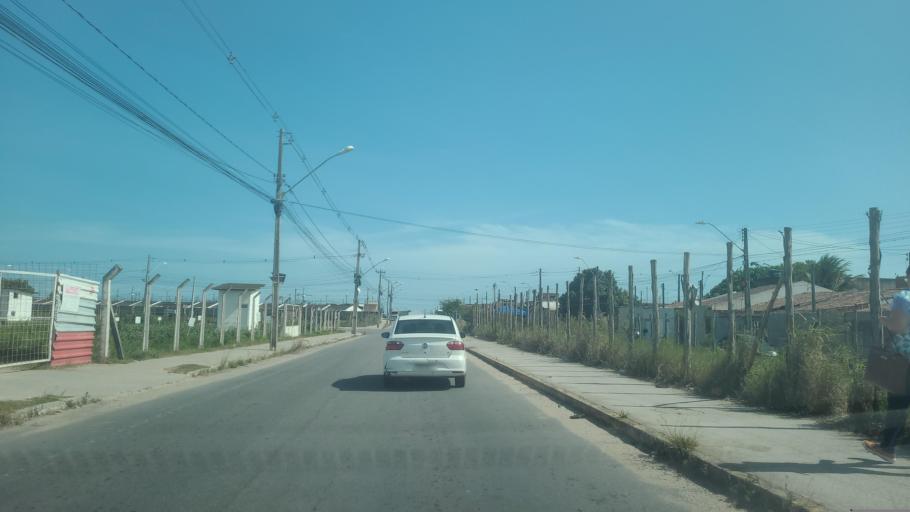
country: BR
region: Alagoas
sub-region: Satuba
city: Satuba
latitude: -9.5308
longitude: -35.7751
